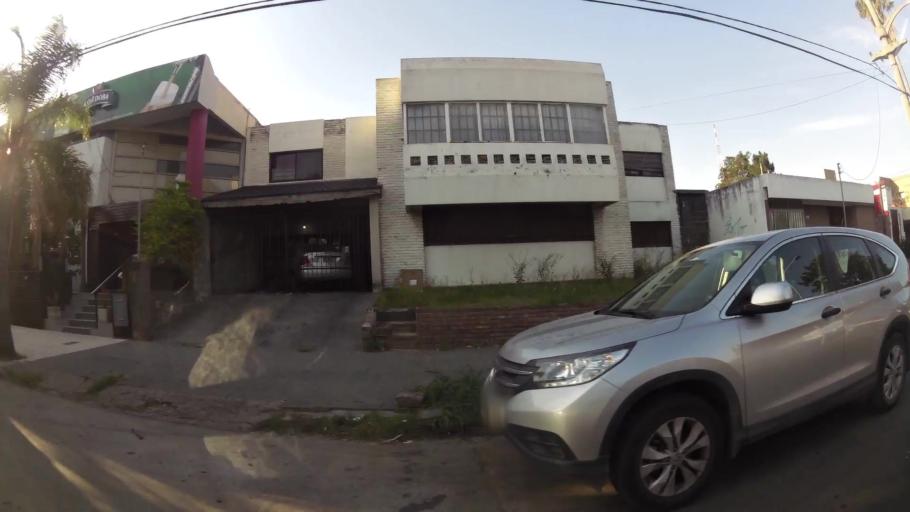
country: AR
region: Cordoba
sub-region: Departamento de Capital
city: Cordoba
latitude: -31.3866
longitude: -64.2271
